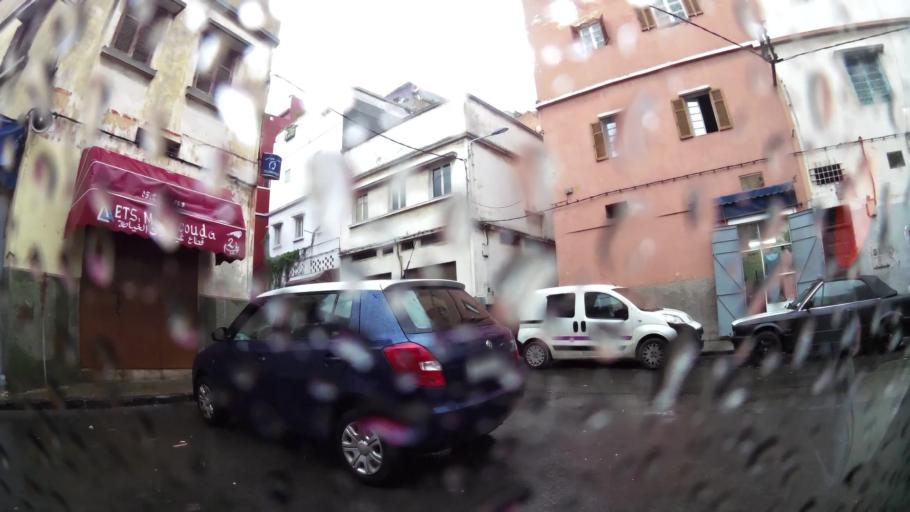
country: MA
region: Grand Casablanca
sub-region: Casablanca
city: Casablanca
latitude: 33.5648
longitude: -7.6059
